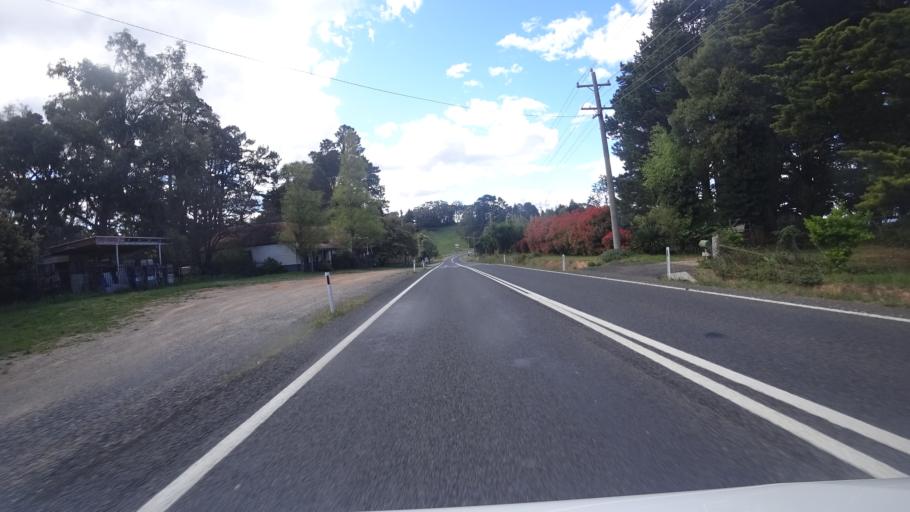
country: AU
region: New South Wales
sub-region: Lithgow
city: Bowenfels
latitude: -33.6464
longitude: 150.0479
